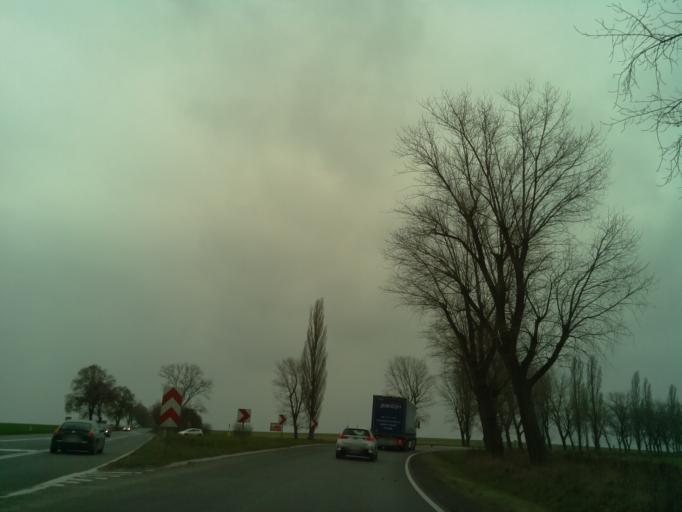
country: PL
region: Lower Silesian Voivodeship
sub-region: Powiat swidnicki
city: Stanowice
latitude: 50.9225
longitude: 16.3684
